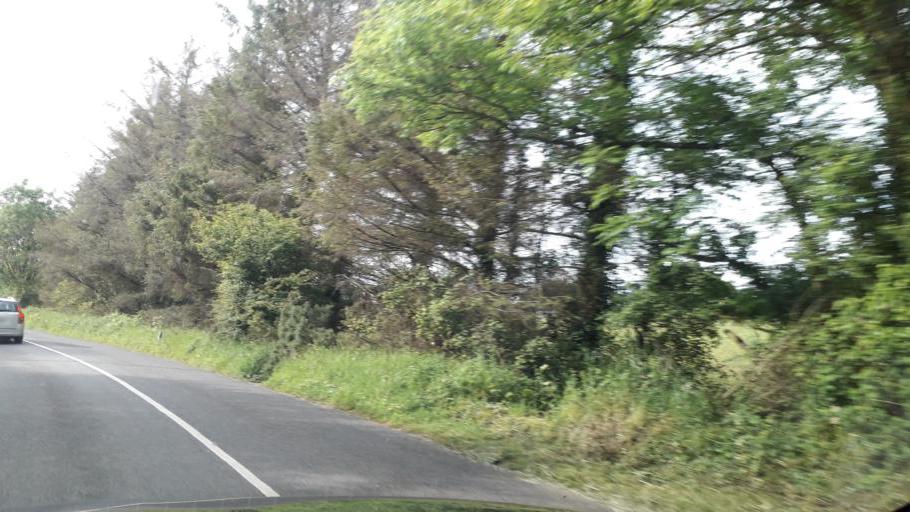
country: IE
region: Leinster
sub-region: Loch Garman
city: Courtown
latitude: 52.5686
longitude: -6.2296
